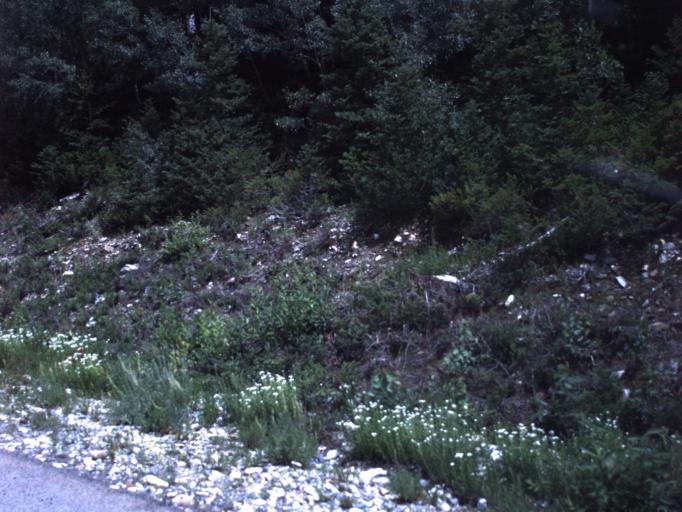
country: US
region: Utah
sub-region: Summit County
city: Snyderville
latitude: 40.5821
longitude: -111.6507
